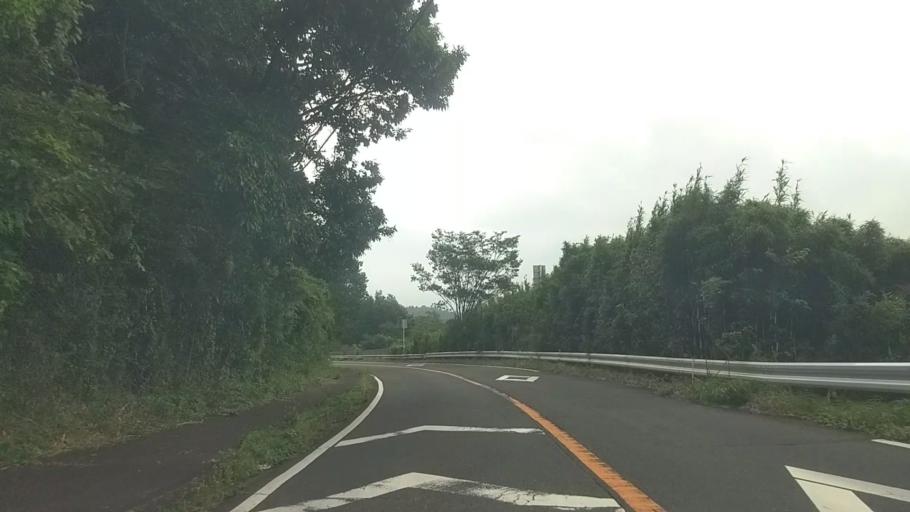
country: JP
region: Chiba
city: Kawaguchi
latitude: 35.2636
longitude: 140.0581
